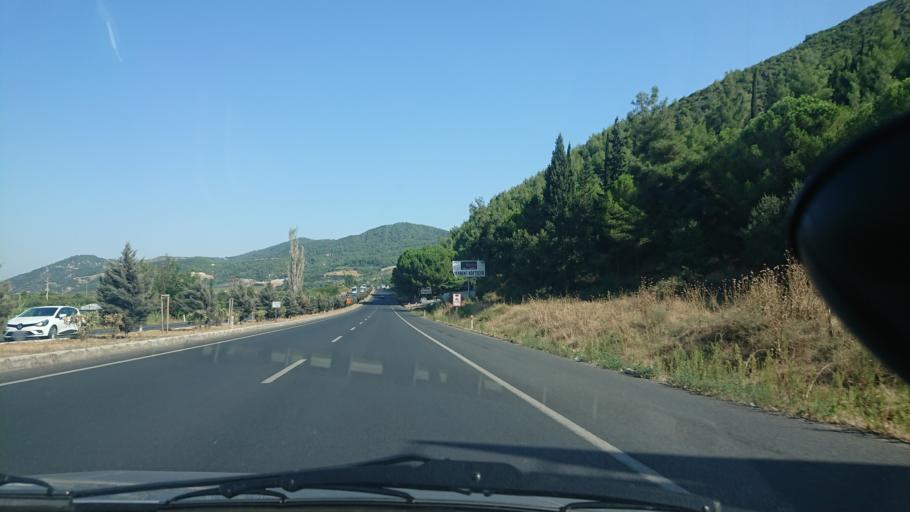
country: TR
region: Manisa
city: Turgutlu
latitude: 38.4866
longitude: 27.8038
